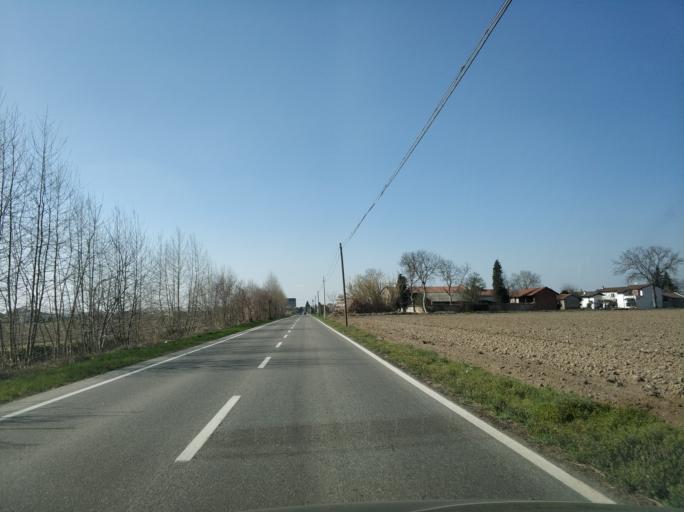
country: IT
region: Piedmont
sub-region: Provincia di Vercelli
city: Borgo Vercelli
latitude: 45.3318
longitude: 8.4579
